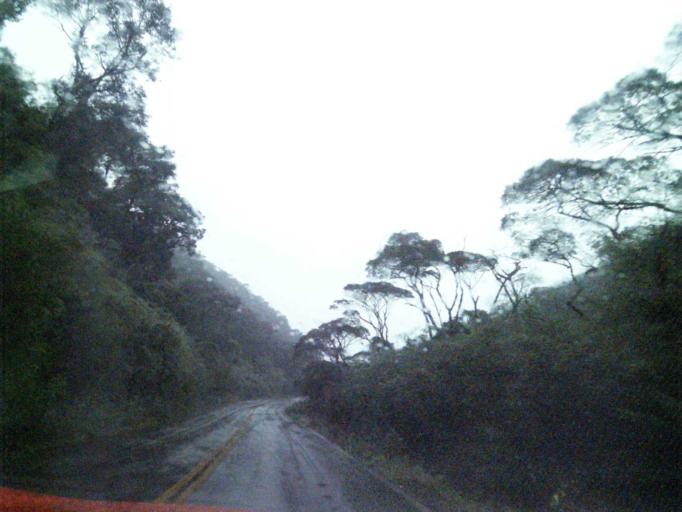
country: BR
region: Santa Catarina
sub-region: Anitapolis
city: Anitapolis
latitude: -27.7639
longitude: -49.0391
